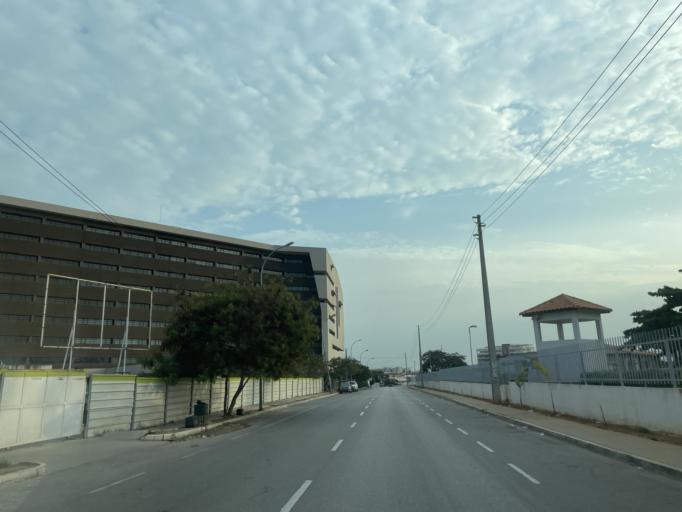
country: AO
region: Luanda
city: Luanda
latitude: -8.9176
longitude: 13.1852
